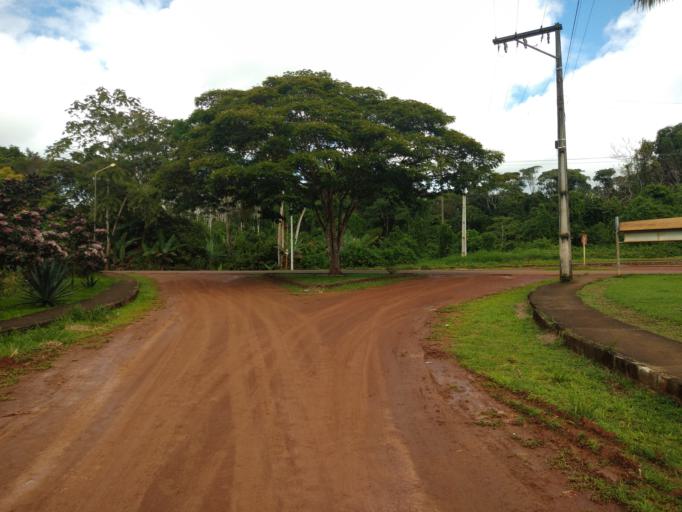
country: BR
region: Bahia
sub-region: Itubera
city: Itubera
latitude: -13.8144
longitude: -39.1472
